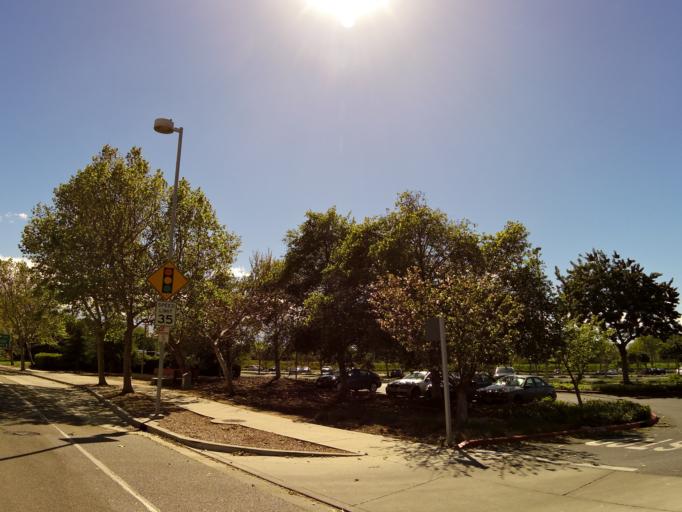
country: US
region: California
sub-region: Santa Clara County
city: Milpitas
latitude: 37.4279
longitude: -121.9244
